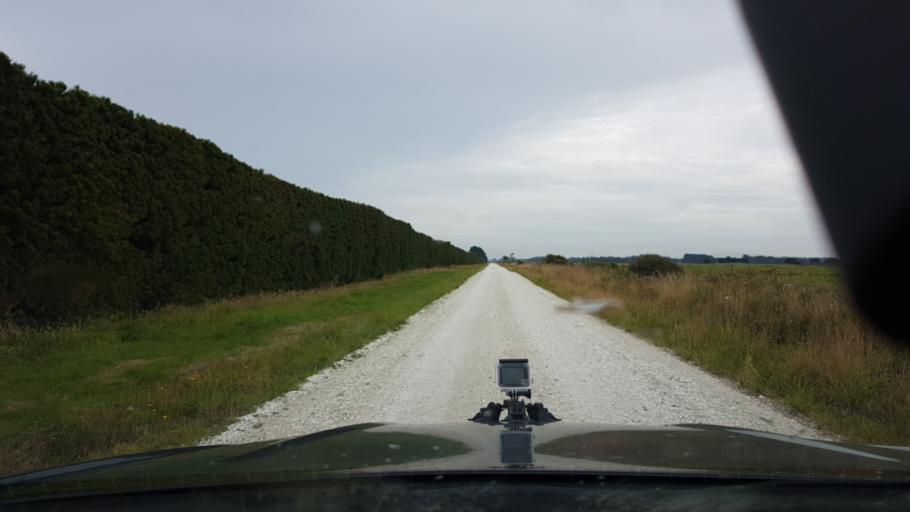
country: NZ
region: Southland
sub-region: Invercargill City
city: Invercargill
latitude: -46.4968
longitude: 168.4178
